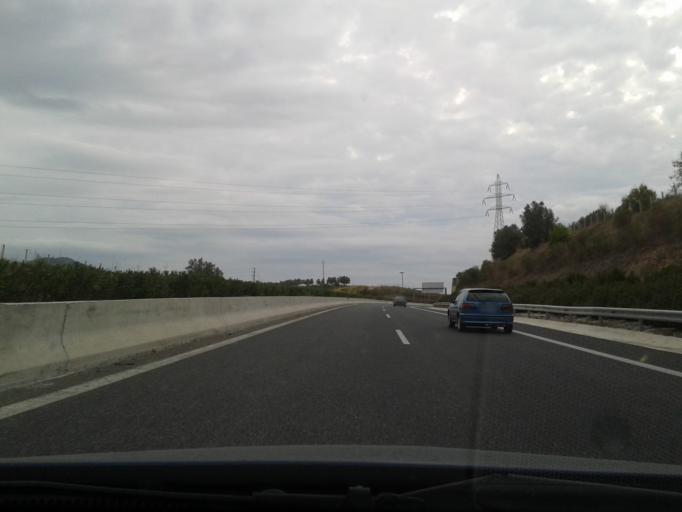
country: GR
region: Peloponnese
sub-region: Nomos Korinthias
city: Arkhaia Korinthos
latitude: 37.9084
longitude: 22.9063
